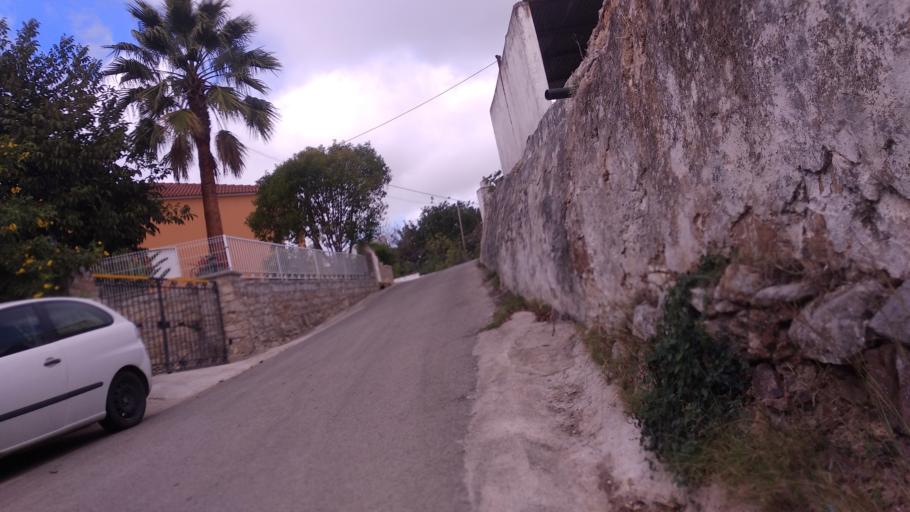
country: PT
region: Faro
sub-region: Sao Bras de Alportel
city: Sao Bras de Alportel
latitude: 37.1632
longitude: -7.9059
